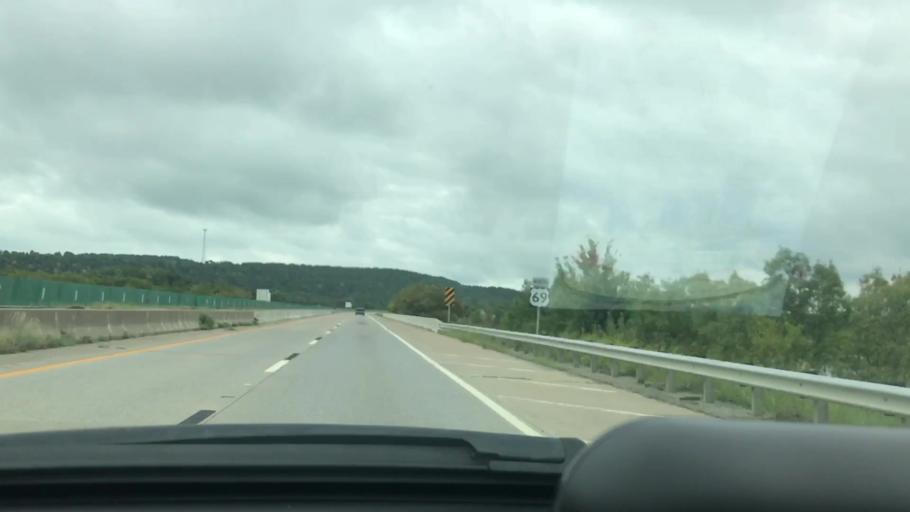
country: US
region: Oklahoma
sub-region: Pittsburg County
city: Krebs
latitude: 35.1051
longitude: -95.6950
